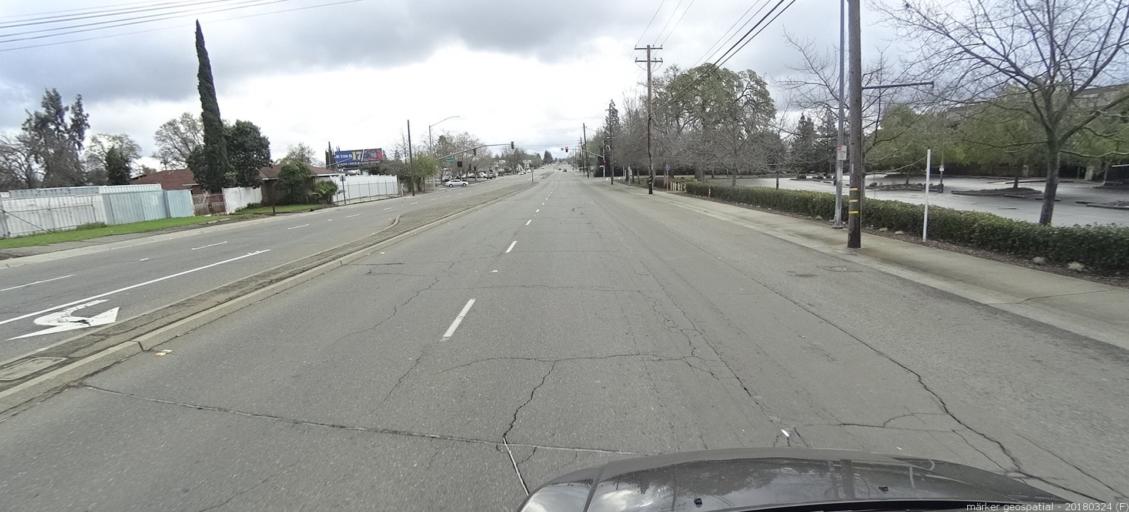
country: US
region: California
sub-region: Sacramento County
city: North Highlands
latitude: 38.6612
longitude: -121.3780
